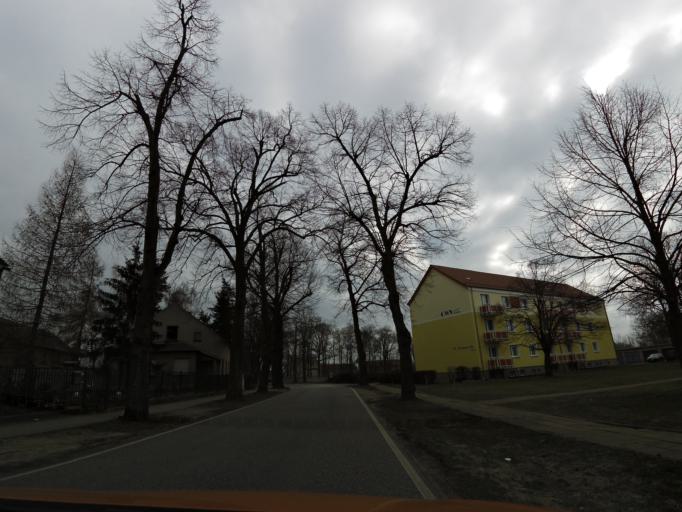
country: DE
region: Brandenburg
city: Ketzin
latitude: 52.4702
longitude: 12.8600
